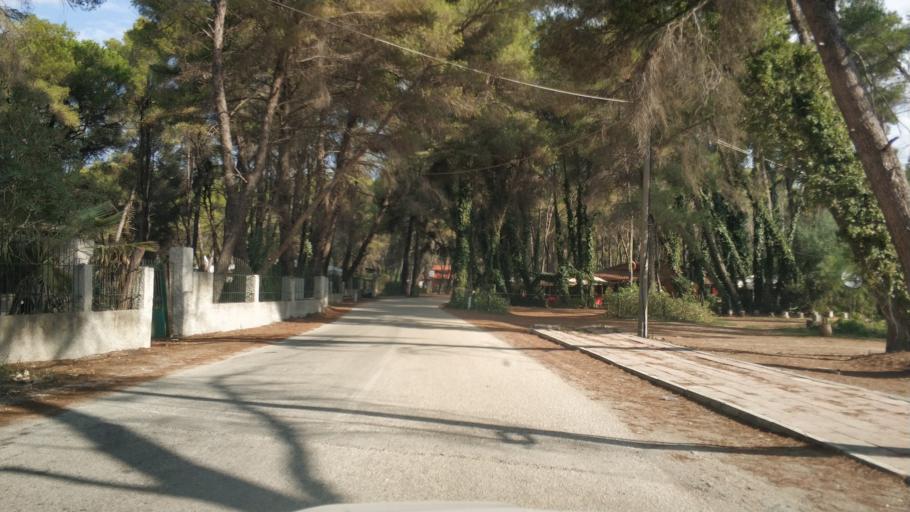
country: AL
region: Fier
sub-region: Rrethi i Lushnjes
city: Divjake
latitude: 40.9734
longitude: 19.4805
